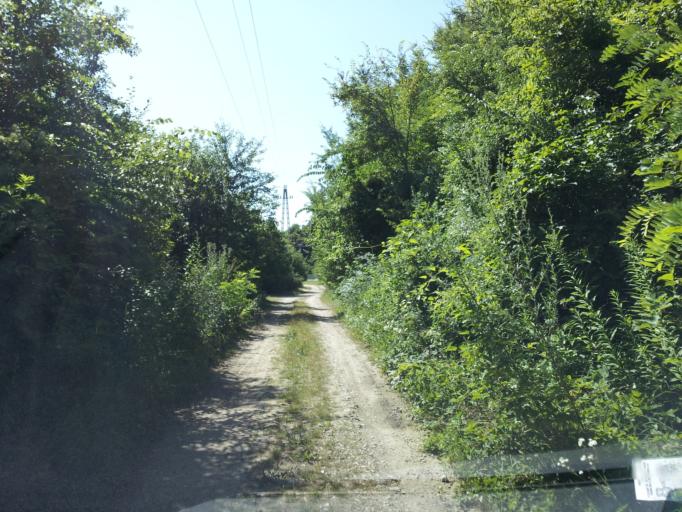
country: HU
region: Veszprem
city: Balatonkenese
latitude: 47.0227
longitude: 18.1625
